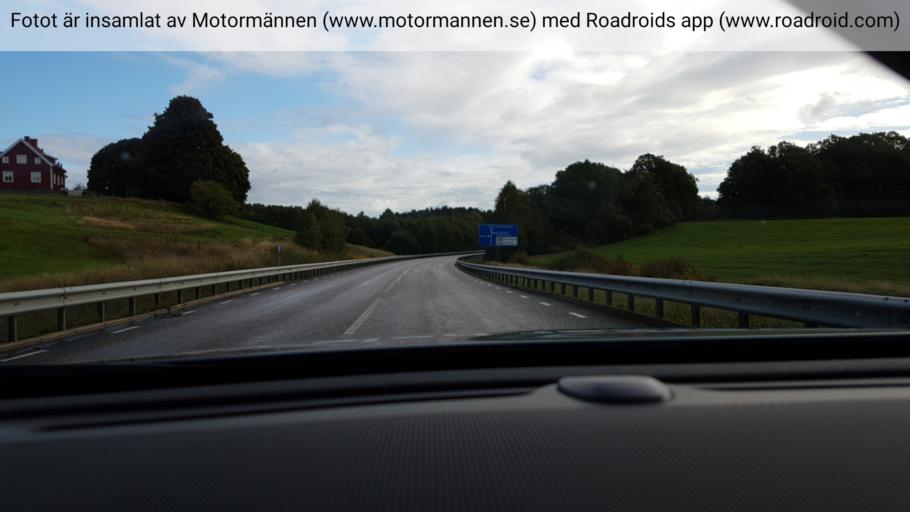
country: SE
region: Vaestra Goetaland
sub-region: Marks Kommun
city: Kinna
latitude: 57.4789
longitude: 12.6956
